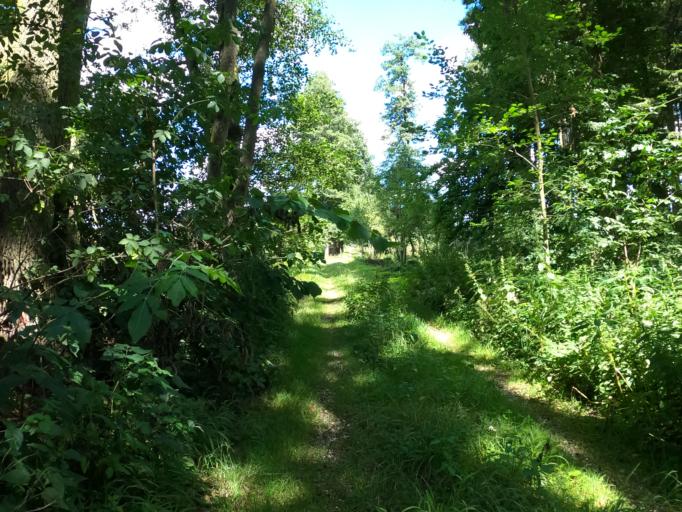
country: DE
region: Bavaria
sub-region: Swabia
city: Bubesheim
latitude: 48.4132
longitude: 10.2233
